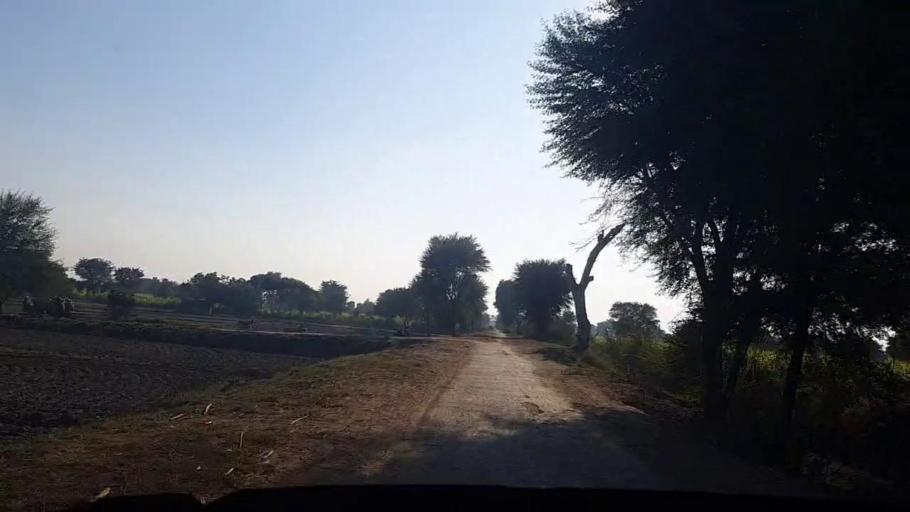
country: PK
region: Sindh
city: Gambat
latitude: 27.3507
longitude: 68.4514
